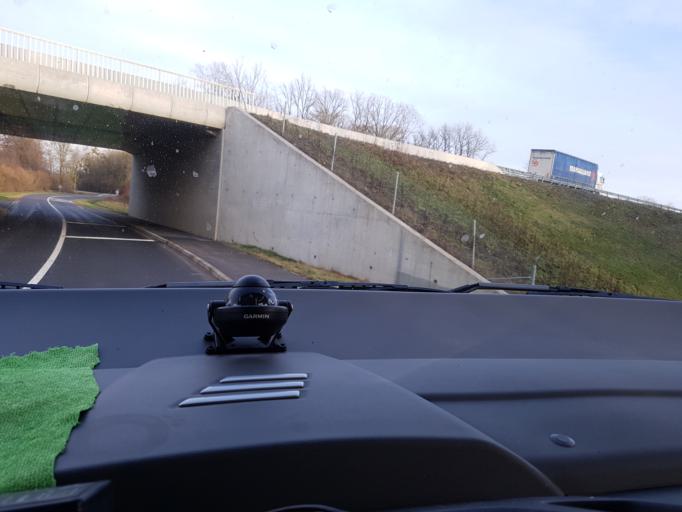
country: FR
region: Champagne-Ardenne
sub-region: Departement des Ardennes
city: Warcq
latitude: 49.7617
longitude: 4.6485
